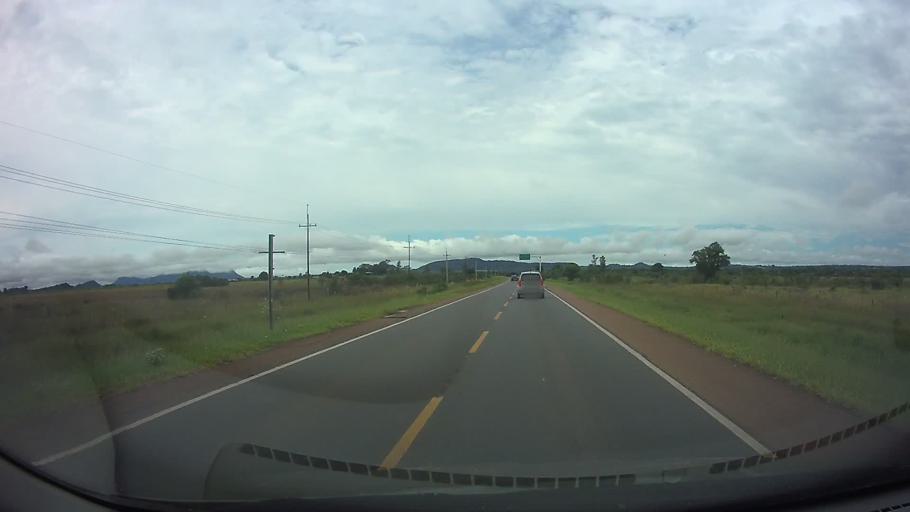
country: PY
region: Paraguari
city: Carapegua
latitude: -25.7384
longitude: -57.2108
